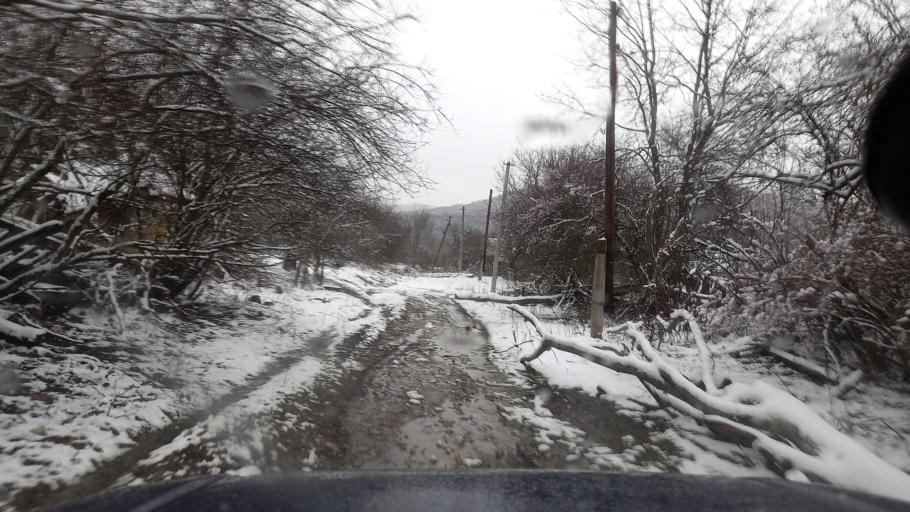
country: RU
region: Adygeya
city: Abadzekhskaya
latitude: 44.3547
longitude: 40.4164
